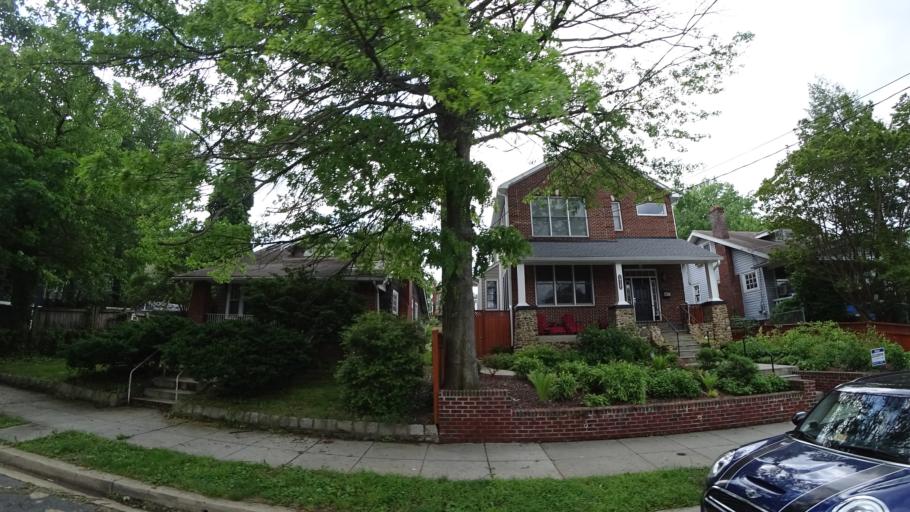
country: US
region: Maryland
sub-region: Prince George's County
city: Mount Rainier
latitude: 38.9311
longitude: -76.9802
